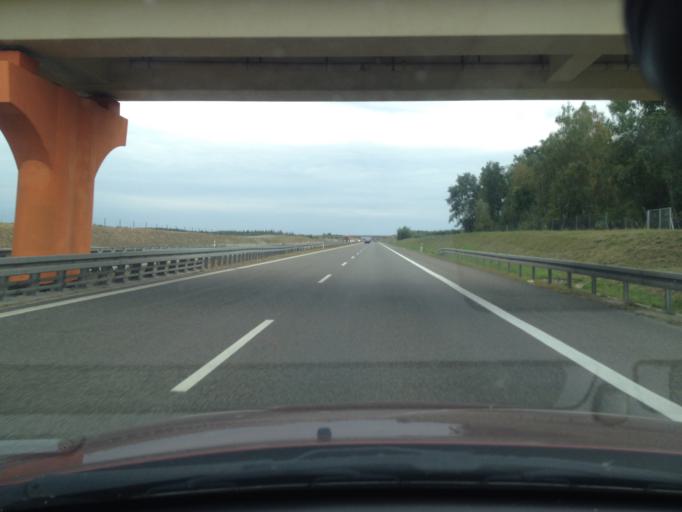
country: PL
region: West Pomeranian Voivodeship
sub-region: Powiat mysliborski
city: Nowogrodek Pomorski
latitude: 52.8974
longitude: 15.0206
